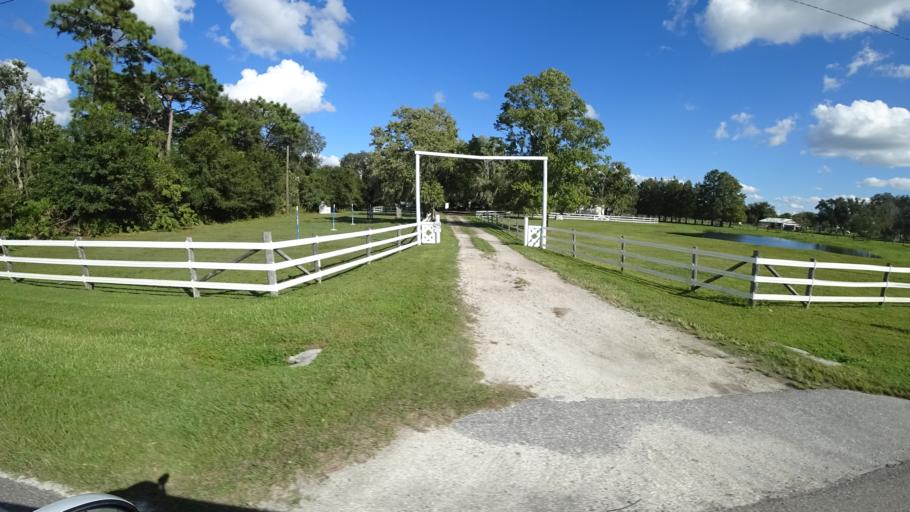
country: US
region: Florida
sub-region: Sarasota County
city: Lake Sarasota
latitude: 27.3420
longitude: -82.2693
